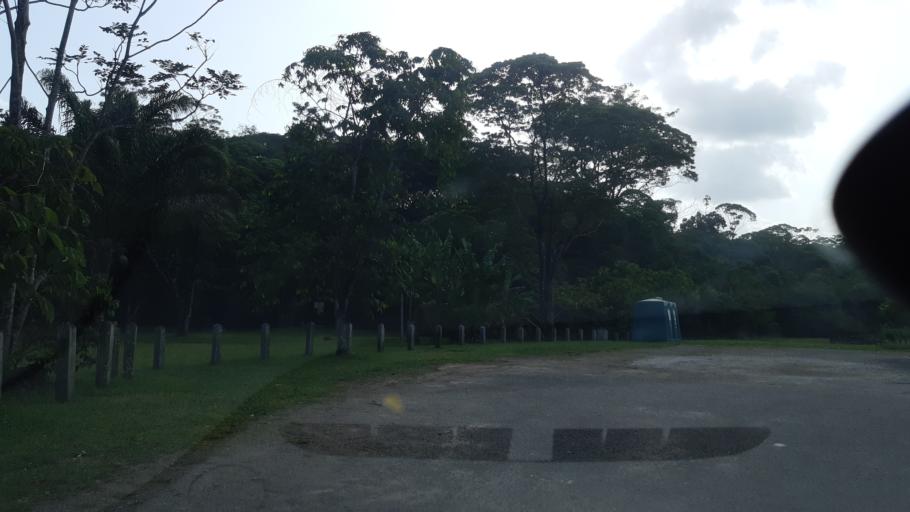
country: GF
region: Guyane
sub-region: Guyane
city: Matoury
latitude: 4.8441
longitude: -52.3260
